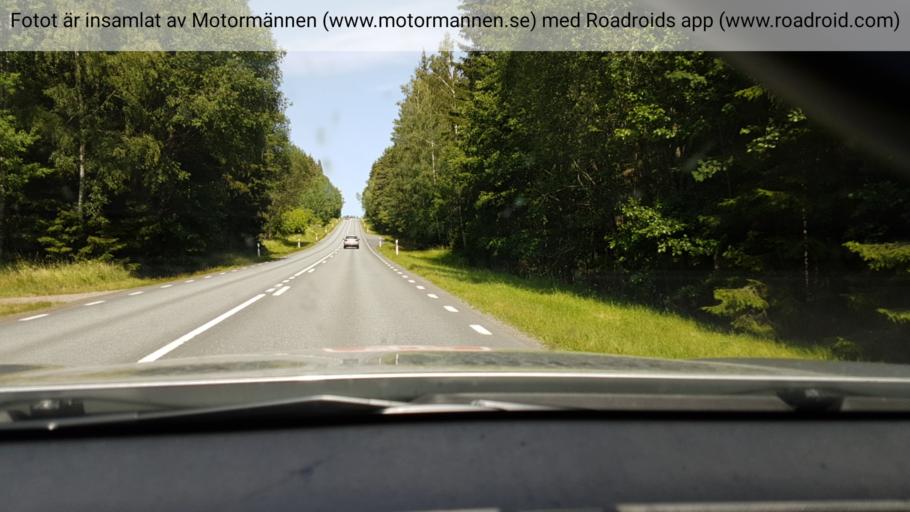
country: SE
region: Joenkoeping
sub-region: Nassjo Kommun
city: Nassjo
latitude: 57.5853
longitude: 14.8235
